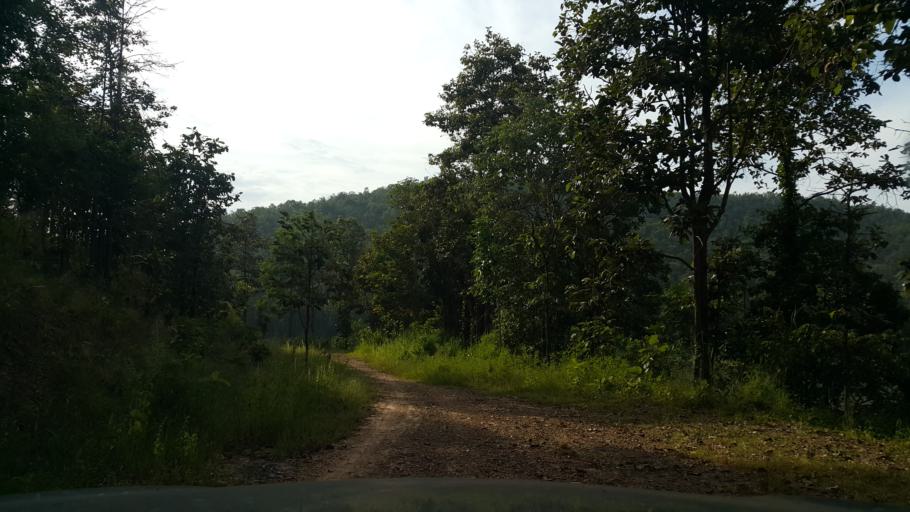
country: TH
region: Chiang Mai
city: San Sai
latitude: 18.9234
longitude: 99.0933
